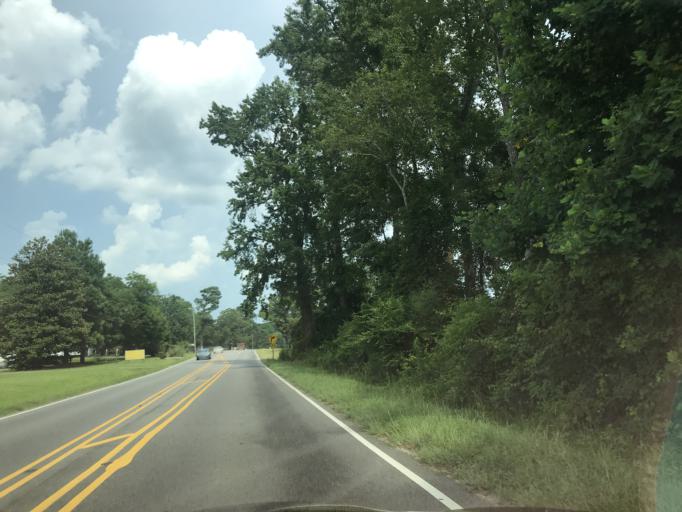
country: US
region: North Carolina
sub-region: Johnston County
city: Four Oaks
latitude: 35.5141
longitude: -78.5382
